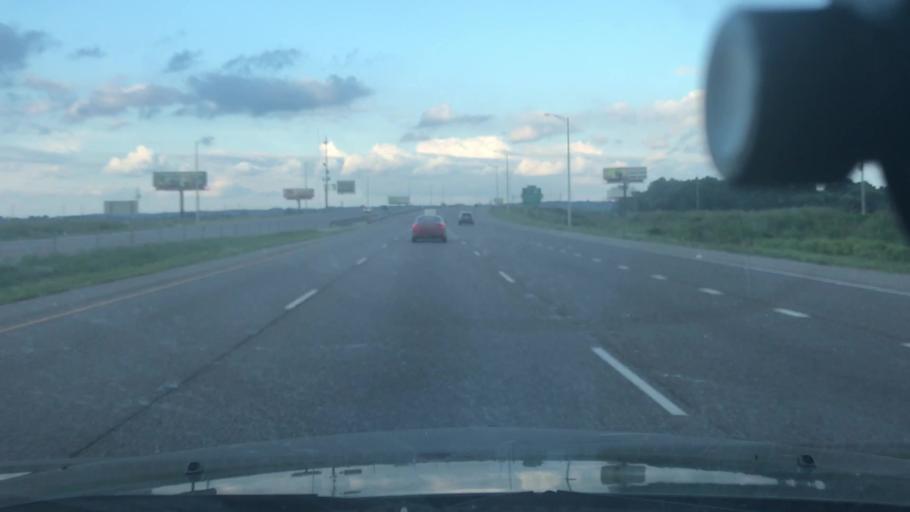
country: US
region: Illinois
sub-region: Saint Clair County
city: Washington Park
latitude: 38.6208
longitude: -90.0870
